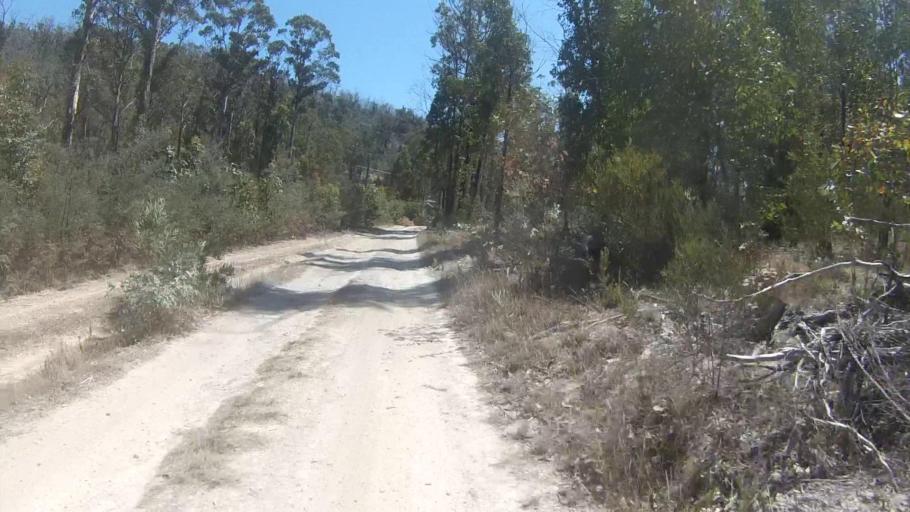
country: AU
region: Tasmania
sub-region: Sorell
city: Sorell
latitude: -42.8235
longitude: 147.6763
